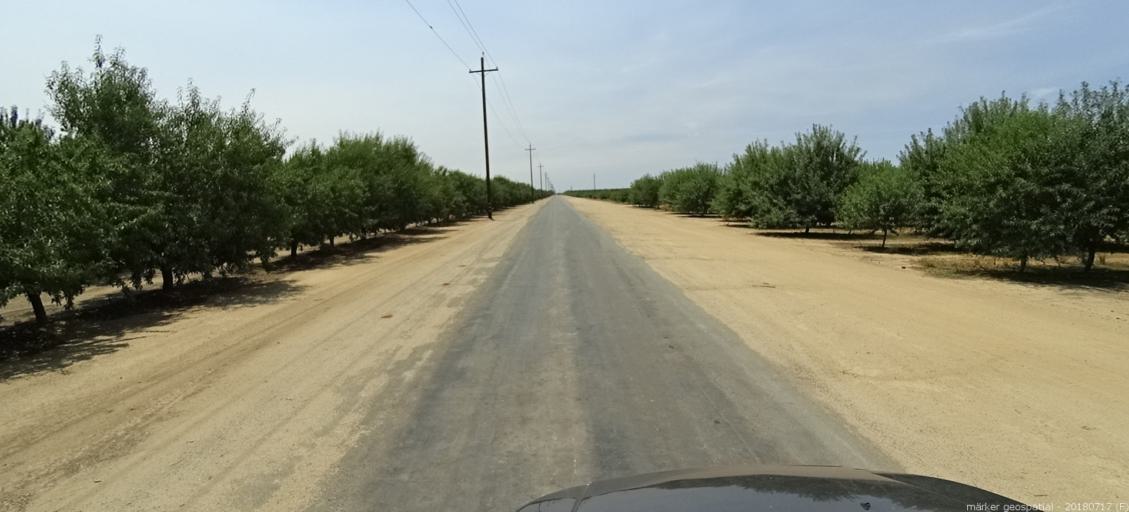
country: US
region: California
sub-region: Madera County
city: Fairmead
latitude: 37.1187
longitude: -120.1658
